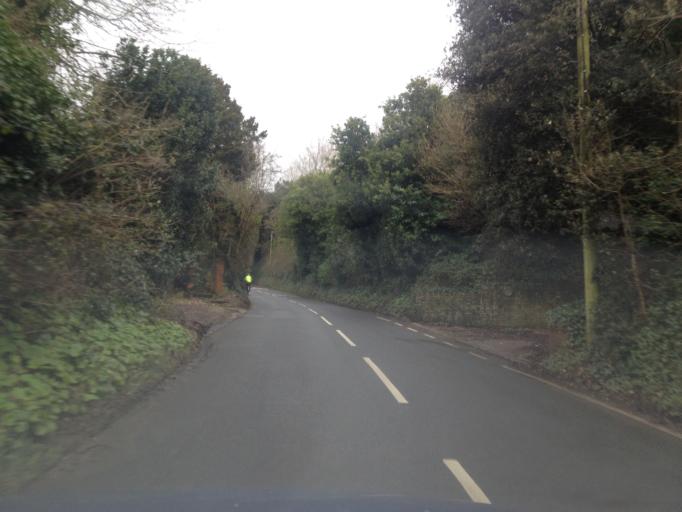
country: GB
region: England
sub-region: Isle of Wight
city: Brading
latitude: 50.6663
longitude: -1.1319
